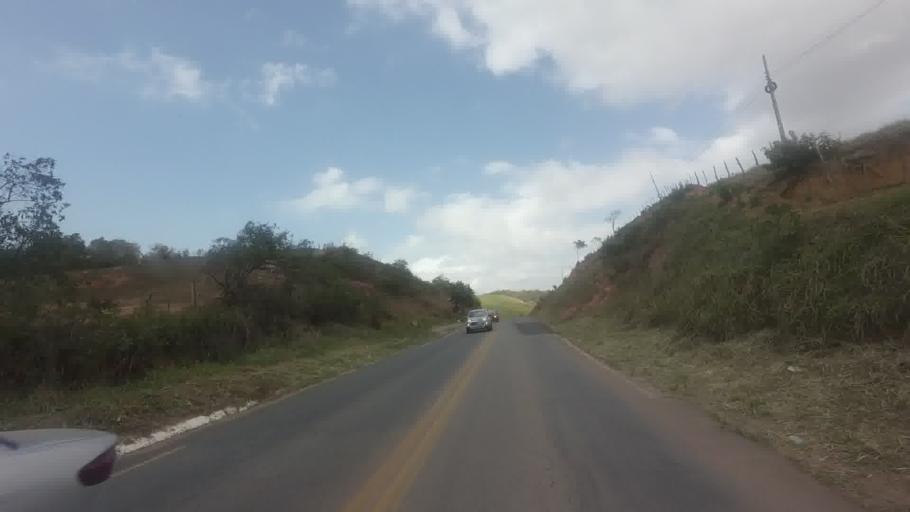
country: BR
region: Espirito Santo
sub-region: Piuma
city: Piuma
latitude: -20.8813
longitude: -40.7666
